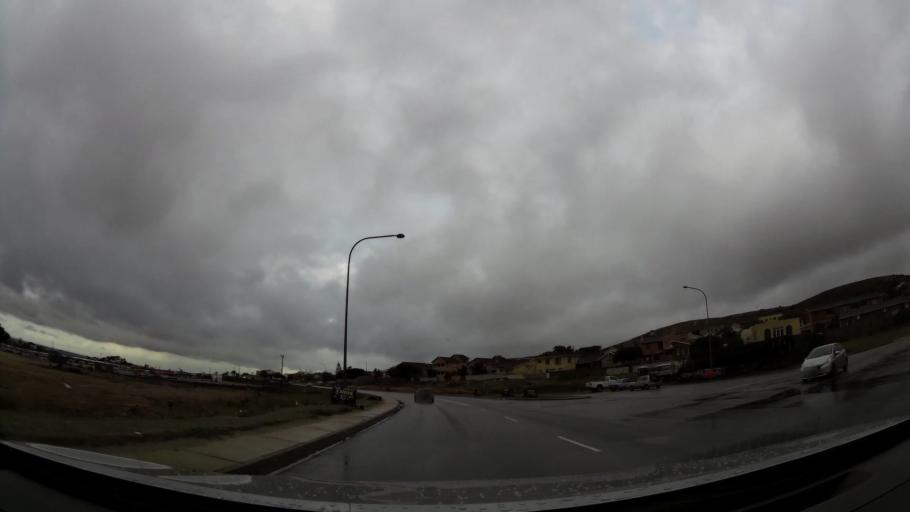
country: ZA
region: Eastern Cape
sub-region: Nelson Mandela Bay Metropolitan Municipality
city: Port Elizabeth
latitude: -33.8899
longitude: 25.5202
